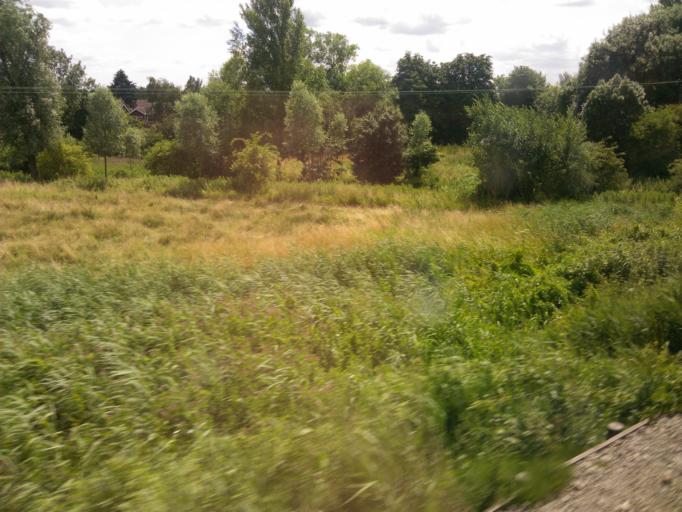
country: GB
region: England
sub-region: Essex
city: Witham
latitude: 51.8200
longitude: 0.6649
